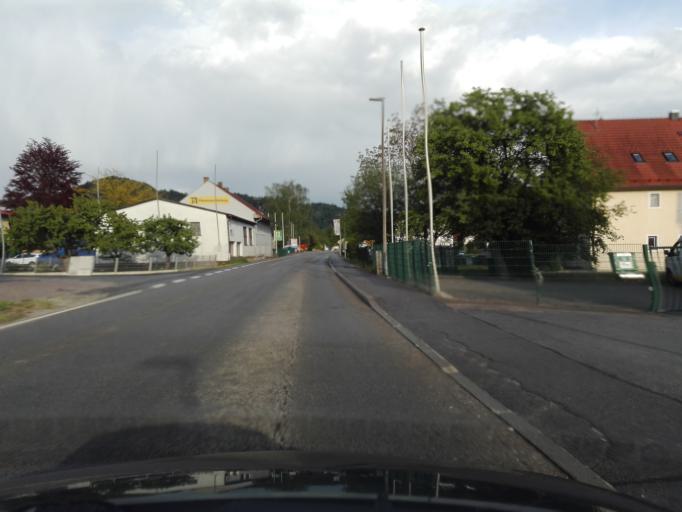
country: DE
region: Bavaria
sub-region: Lower Bavaria
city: Obernzell
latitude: 48.5567
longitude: 13.6278
